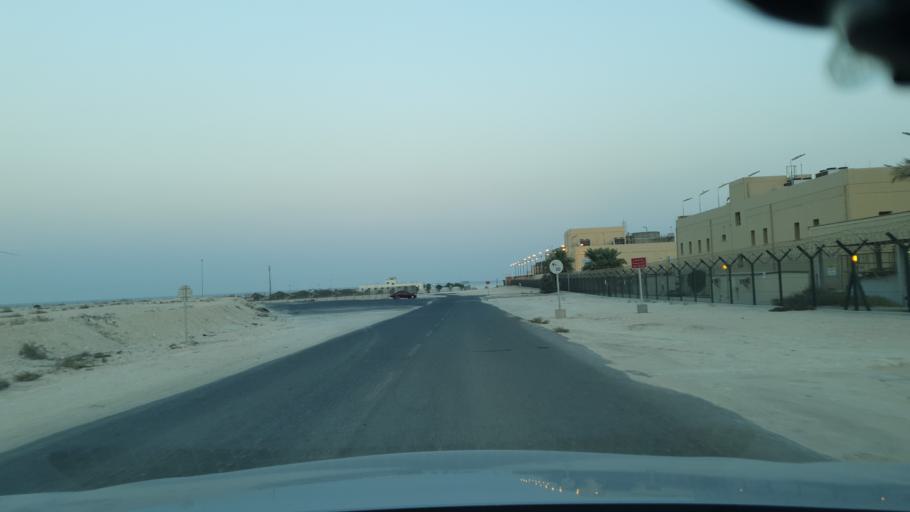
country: BH
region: Central Governorate
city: Dar Kulayb
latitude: 25.9728
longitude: 50.6078
